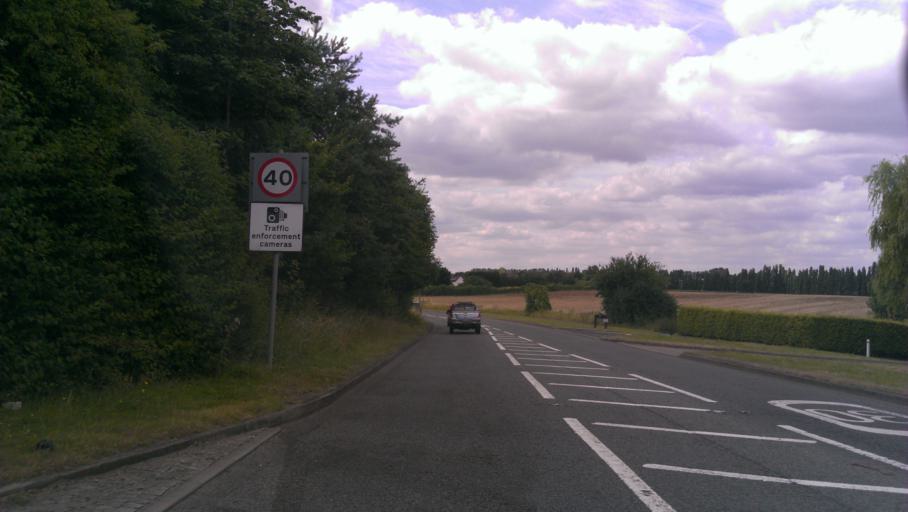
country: GB
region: England
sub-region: Kent
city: Strood
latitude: 51.4111
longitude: 0.4957
